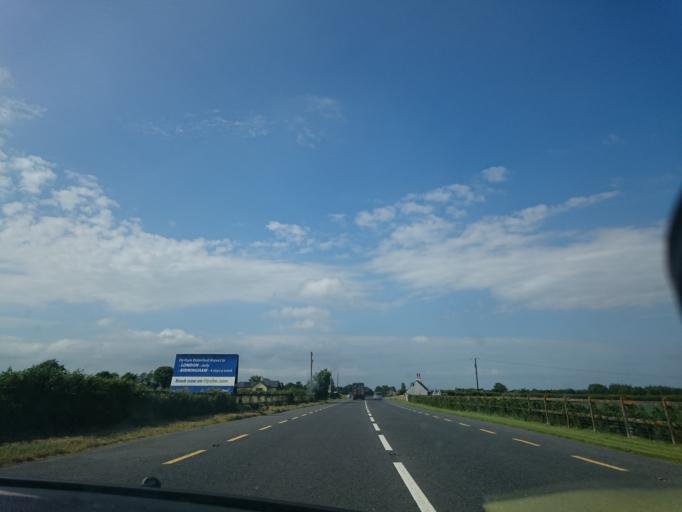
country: IE
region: Leinster
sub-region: Kilkenny
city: Kilkenny
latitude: 52.5875
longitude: -7.2407
